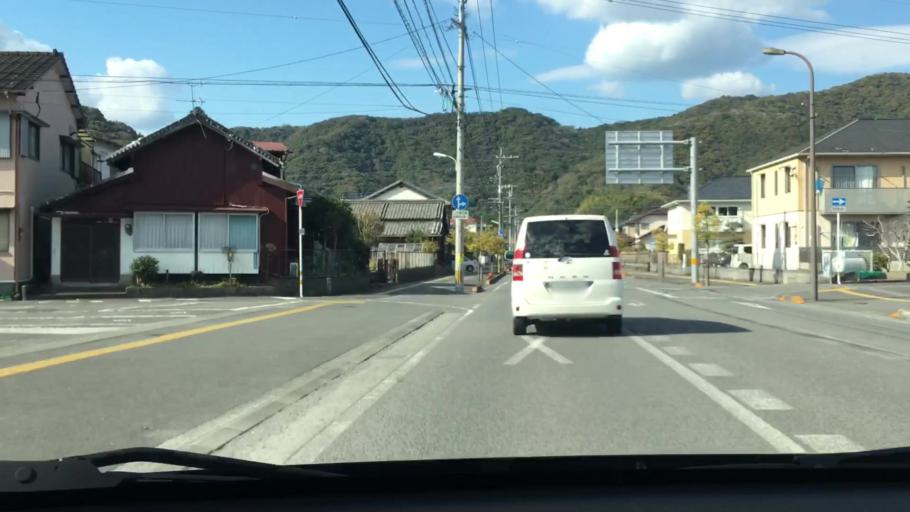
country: JP
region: Oita
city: Saiki
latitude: 32.9619
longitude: 131.8992
